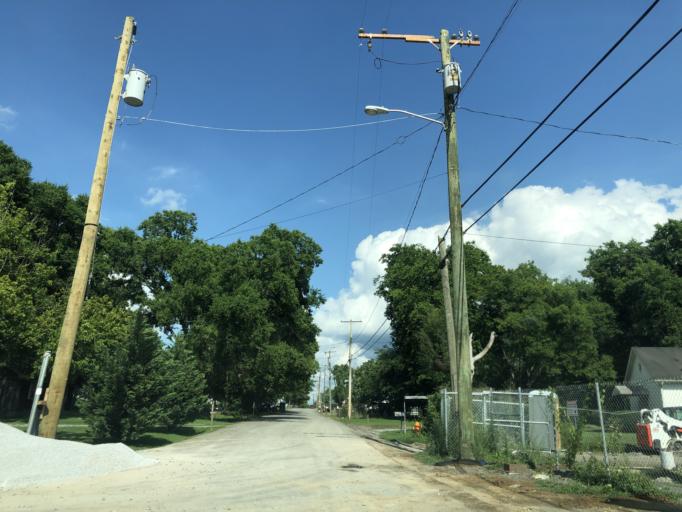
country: US
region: Tennessee
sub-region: Davidson County
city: Nashville
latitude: 36.2074
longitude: -86.7663
